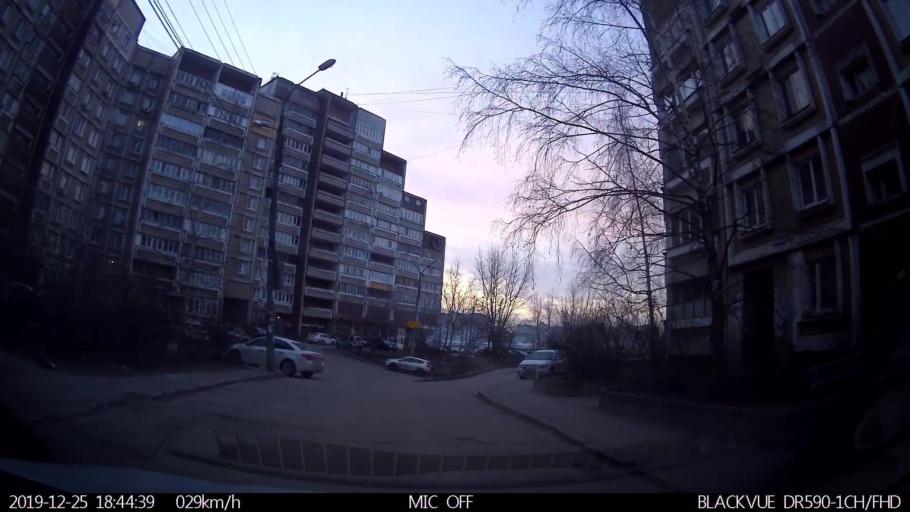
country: RU
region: Nizjnij Novgorod
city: Nizhniy Novgorod
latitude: 56.3456
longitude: 43.9311
